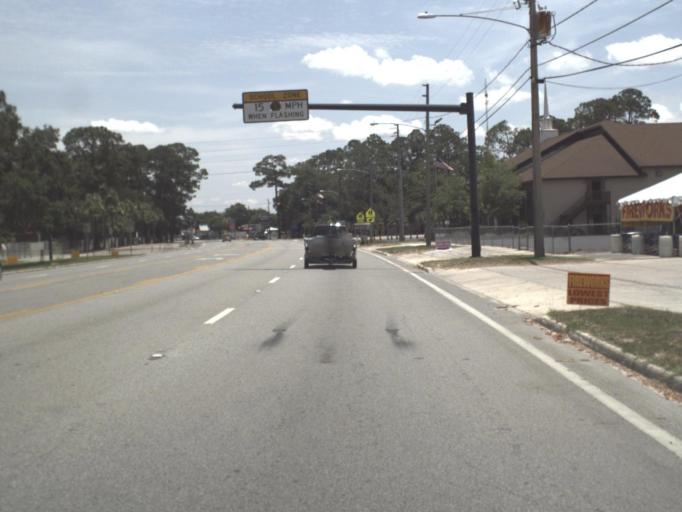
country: US
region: Florida
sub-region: Dixie County
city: Cross City
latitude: 29.6375
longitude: -83.1353
